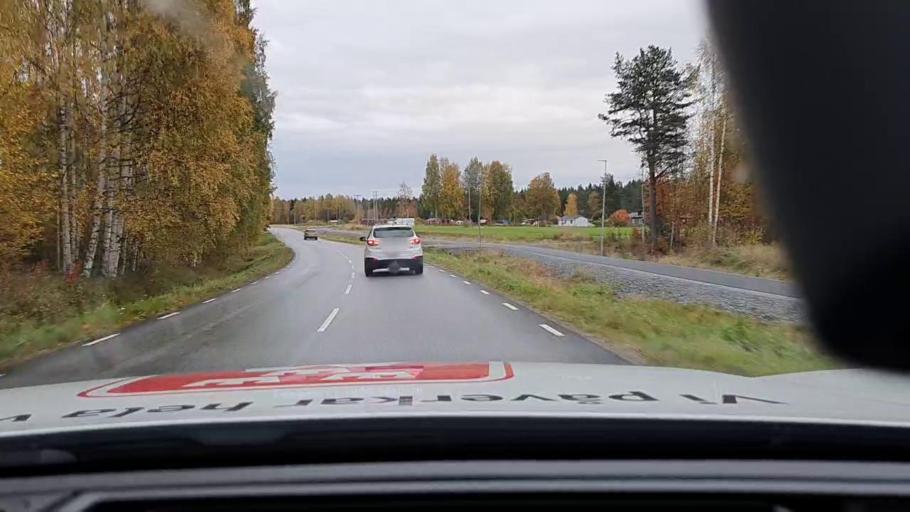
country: SE
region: Norrbotten
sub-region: Bodens Kommun
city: Saevast
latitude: 65.7688
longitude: 21.7078
